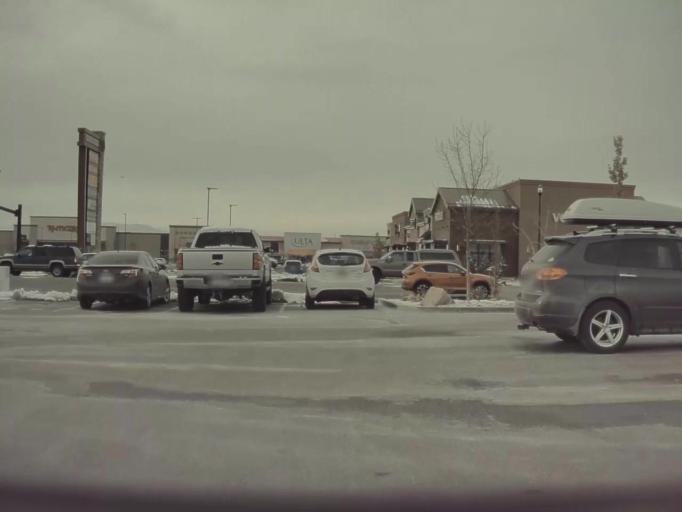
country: US
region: Utah
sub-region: Utah County
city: Spanish Fork
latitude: 40.1254
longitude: -111.6399
